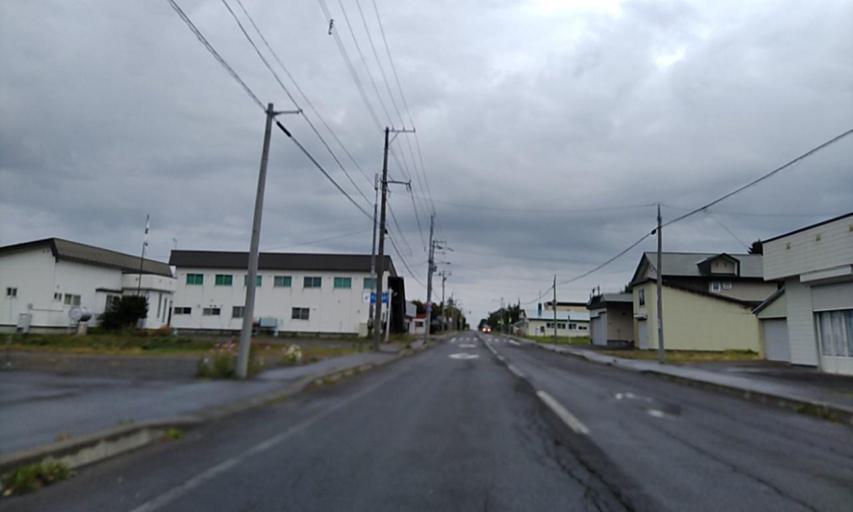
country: JP
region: Hokkaido
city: Nayoro
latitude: 44.6583
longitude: 142.8775
